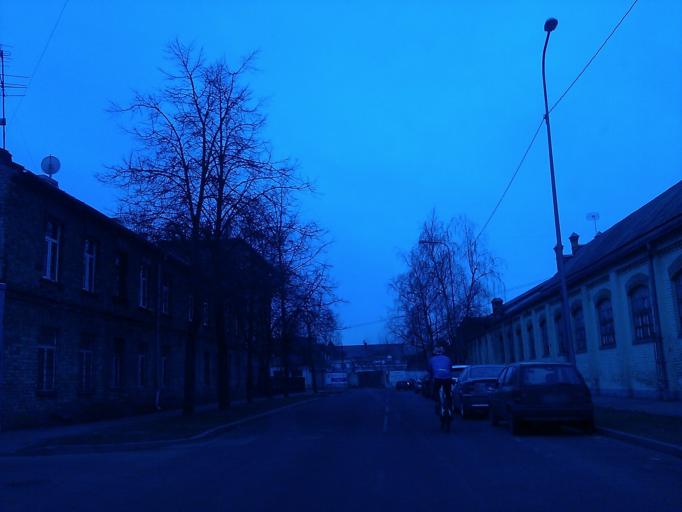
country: LV
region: Riga
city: Riga
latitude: 56.9485
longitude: 24.1489
